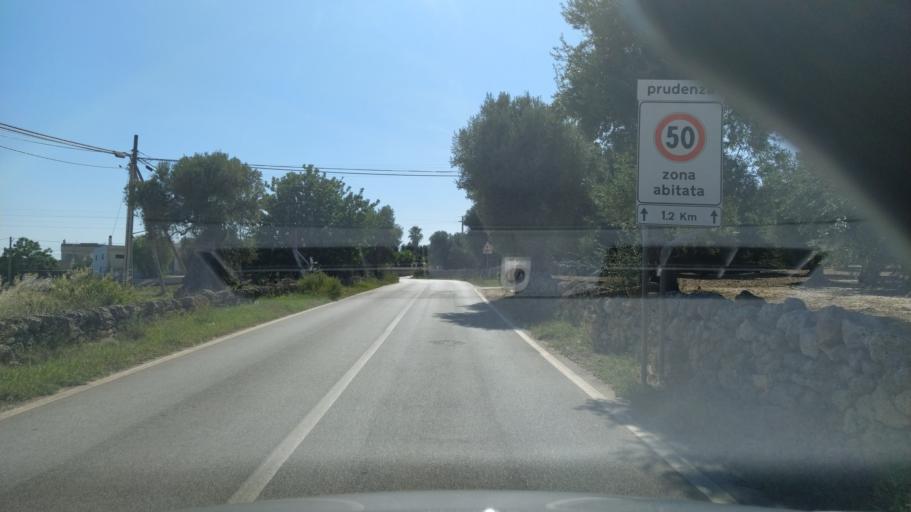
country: IT
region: Apulia
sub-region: Provincia di Brindisi
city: Fasano
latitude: 40.8980
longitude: 17.3525
